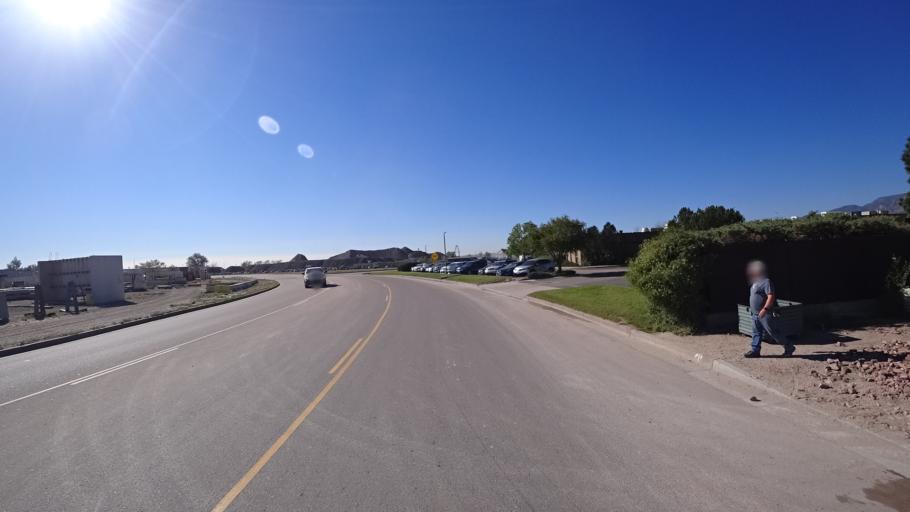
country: US
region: Colorado
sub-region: El Paso County
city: Stratmoor
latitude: 38.7827
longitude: -104.7659
